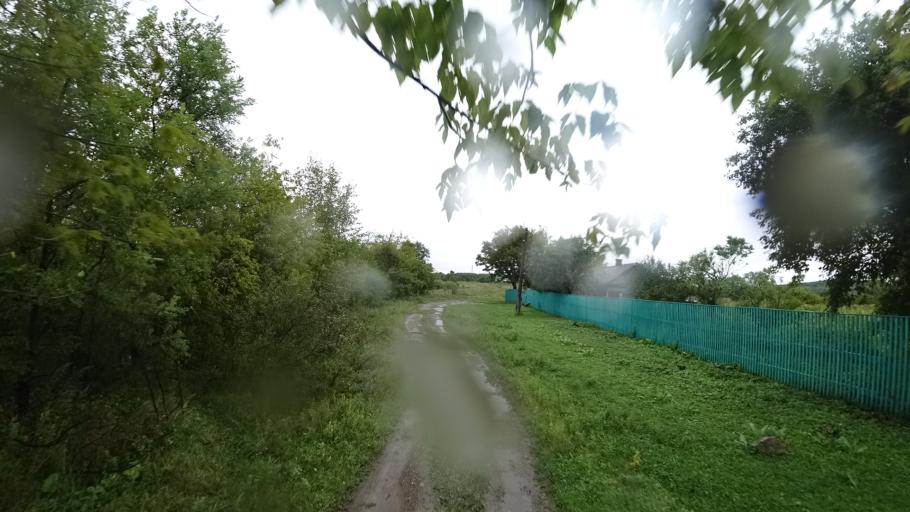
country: RU
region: Primorskiy
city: Monastyrishche
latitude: 44.2615
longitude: 132.4276
